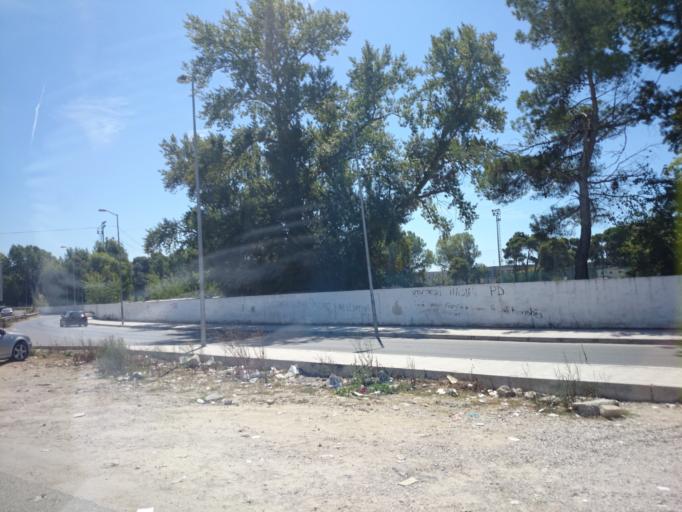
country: AL
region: Durres
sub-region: Rrethi i Durresit
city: Rrashbull
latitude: 41.2915
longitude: 19.5095
